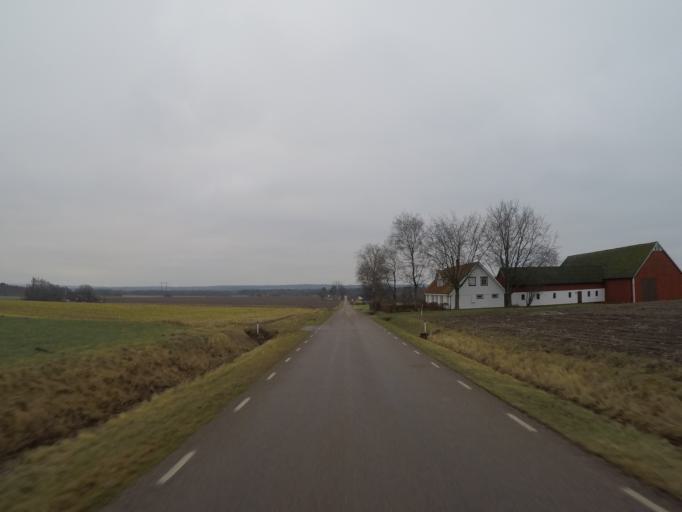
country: SE
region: Skane
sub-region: Hoors Kommun
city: Loberod
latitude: 55.7501
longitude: 13.4174
